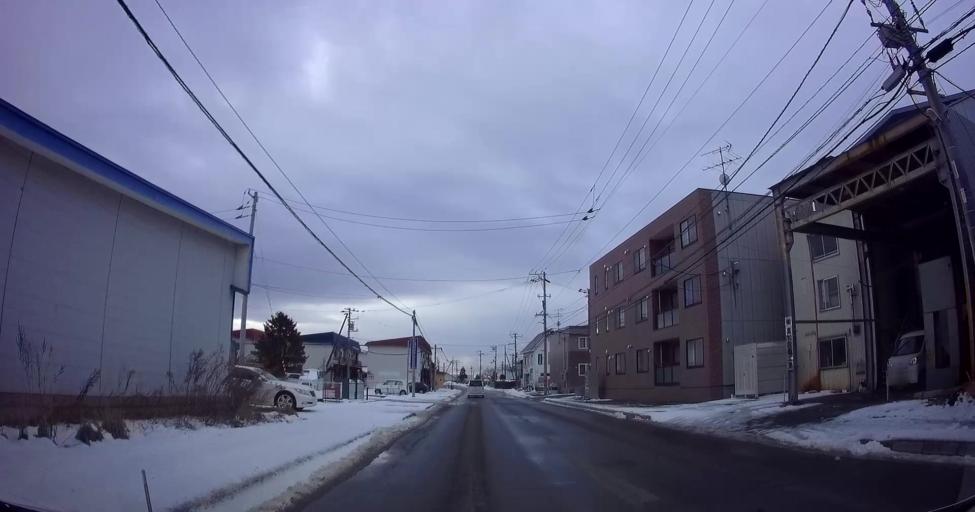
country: JP
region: Hokkaido
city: Kamiiso
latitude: 41.8278
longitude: 140.6864
